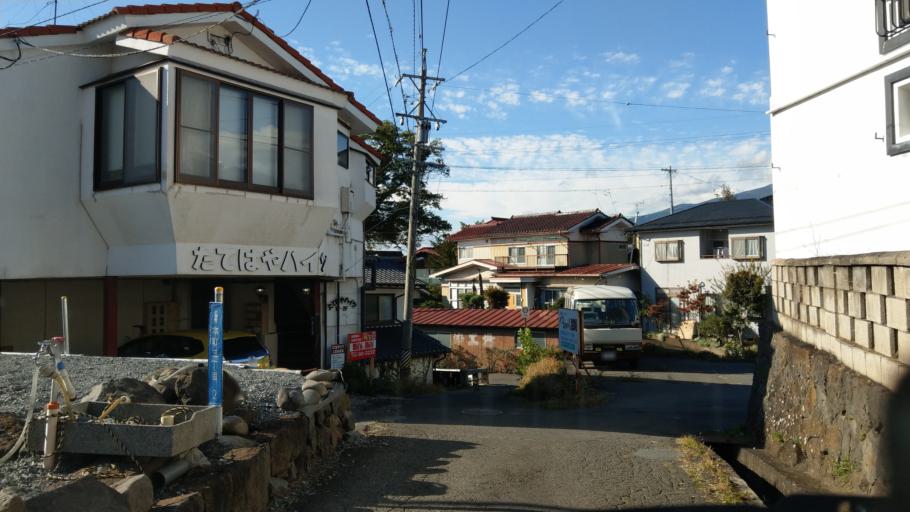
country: JP
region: Nagano
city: Komoro
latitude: 36.3297
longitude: 138.4253
